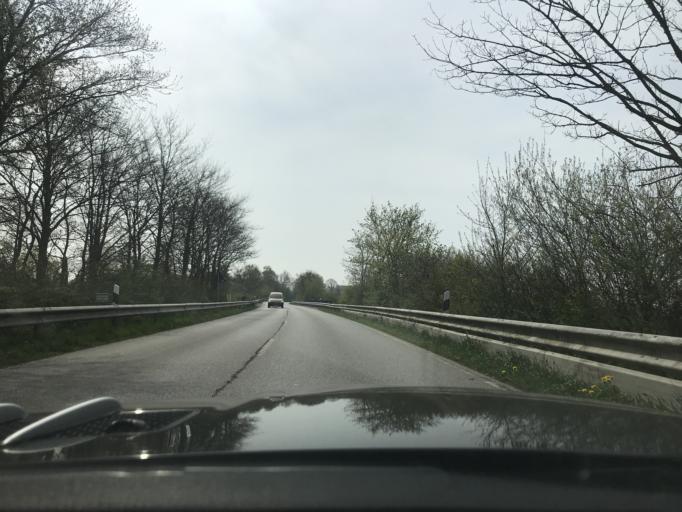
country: DE
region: Schleswig-Holstein
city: Grube
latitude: 54.2425
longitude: 11.0316
